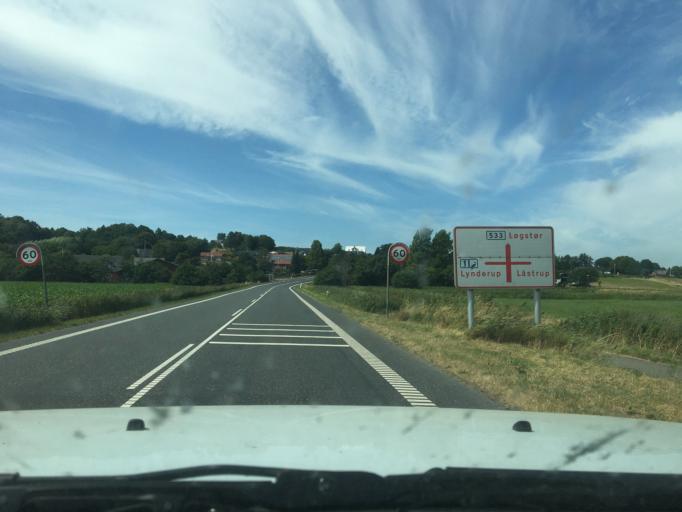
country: DK
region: Central Jutland
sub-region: Viborg Kommune
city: Viborg
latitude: 56.5735
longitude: 9.3792
